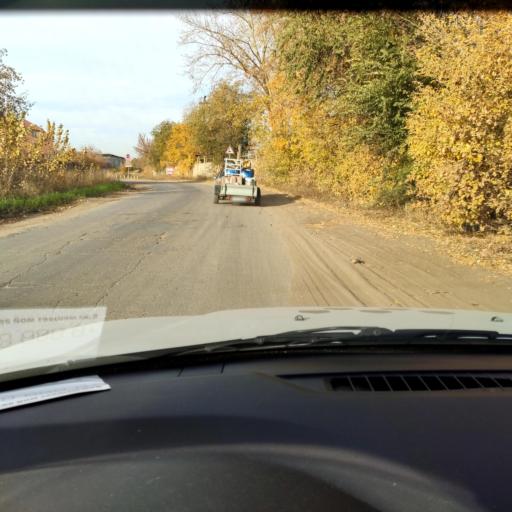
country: RU
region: Samara
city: Zhigulevsk
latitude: 53.4736
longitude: 49.5013
